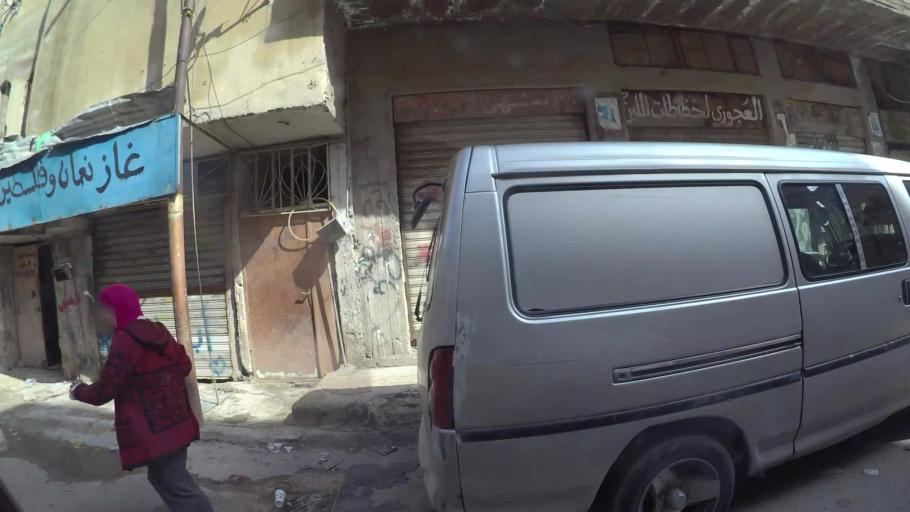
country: JO
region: Amman
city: Al Jubayhah
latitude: 32.0723
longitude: 35.8433
